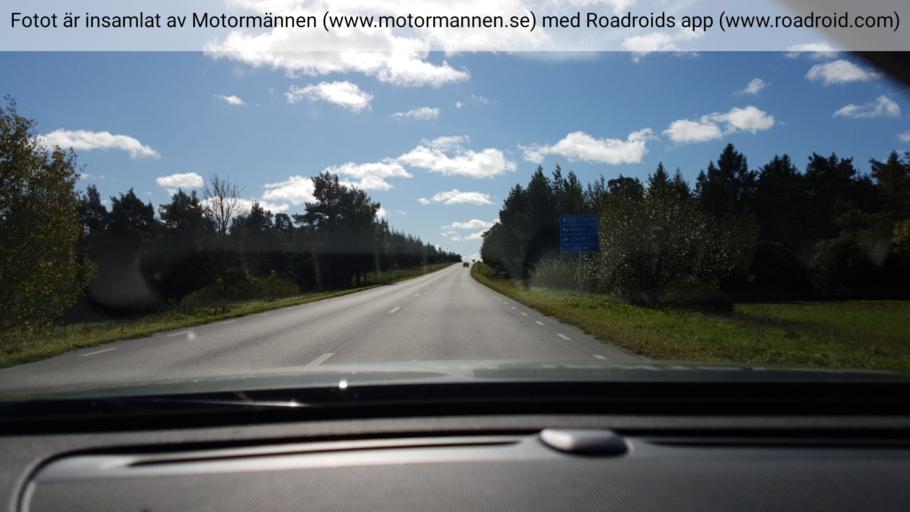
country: SE
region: Gotland
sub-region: Gotland
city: Slite
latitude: 57.7551
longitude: 18.7905
